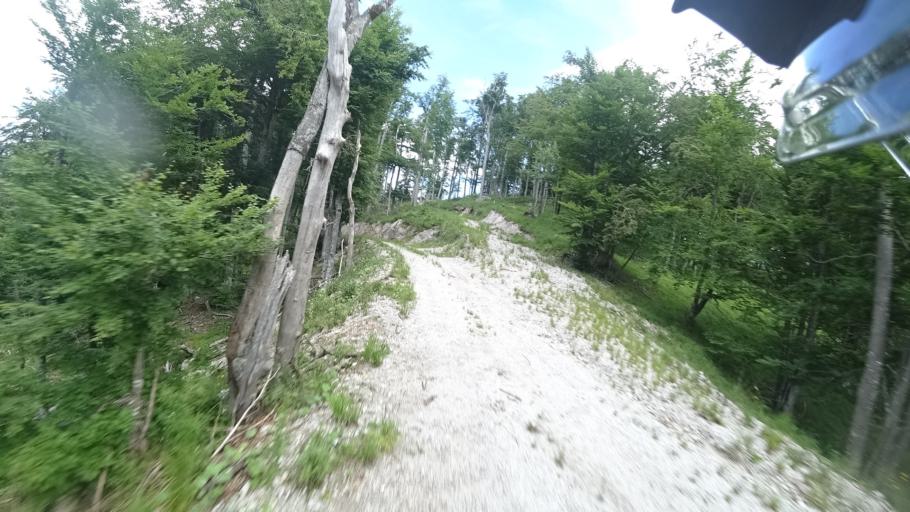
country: SI
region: Osilnica
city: Osilnica
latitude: 45.5090
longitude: 14.6229
